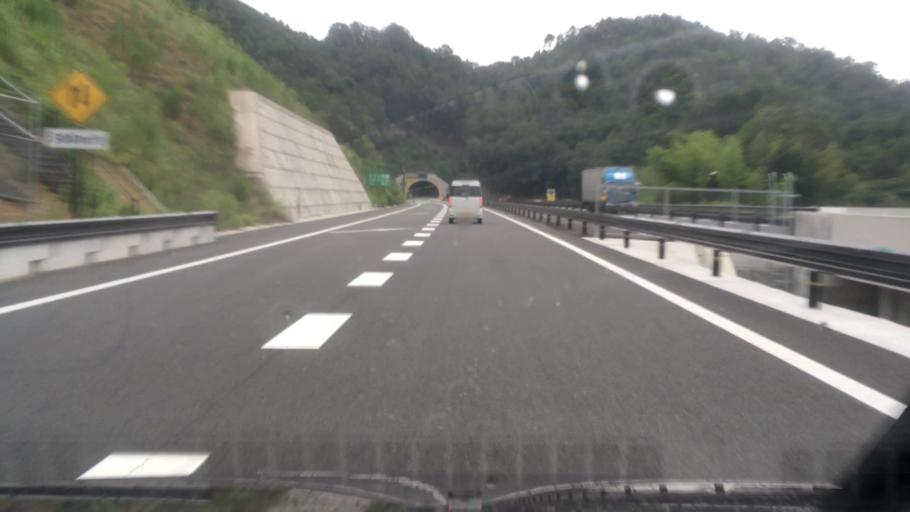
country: JP
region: Hyogo
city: Toyooka
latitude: 35.4321
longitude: 134.7677
